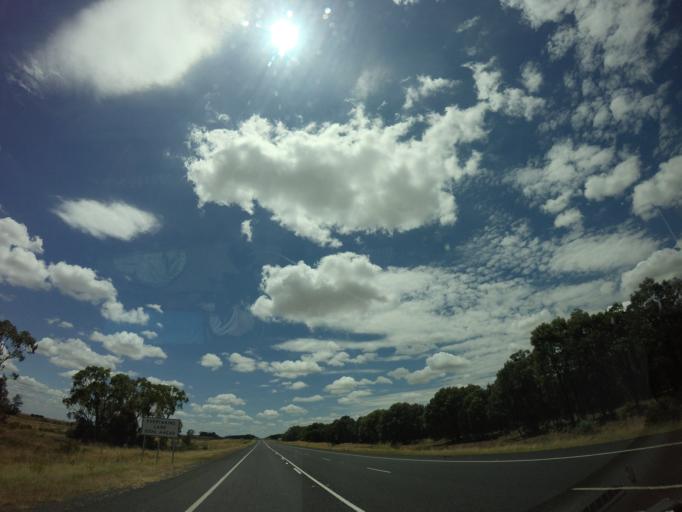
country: AU
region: New South Wales
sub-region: Moree Plains
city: Boggabilla
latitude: -28.8700
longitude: 150.1823
